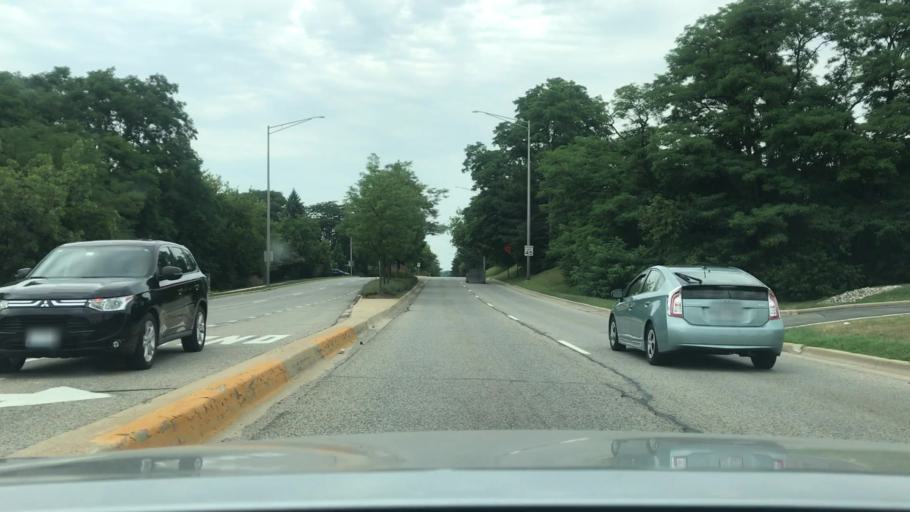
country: US
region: Illinois
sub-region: Will County
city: Bolingbrook
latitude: 41.7126
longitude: -88.0687
